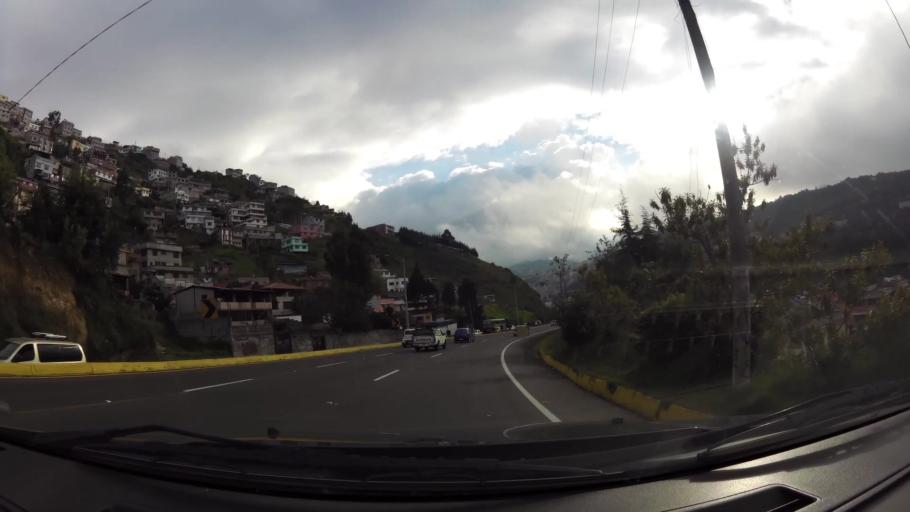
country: EC
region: Pichincha
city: Quito
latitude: -0.2272
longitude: -78.4915
